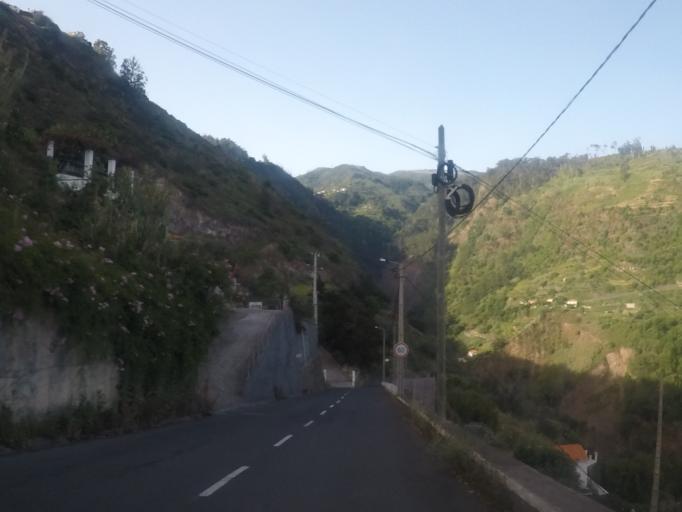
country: PT
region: Madeira
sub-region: Calheta
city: Arco da Calheta
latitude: 32.7079
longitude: -17.1372
